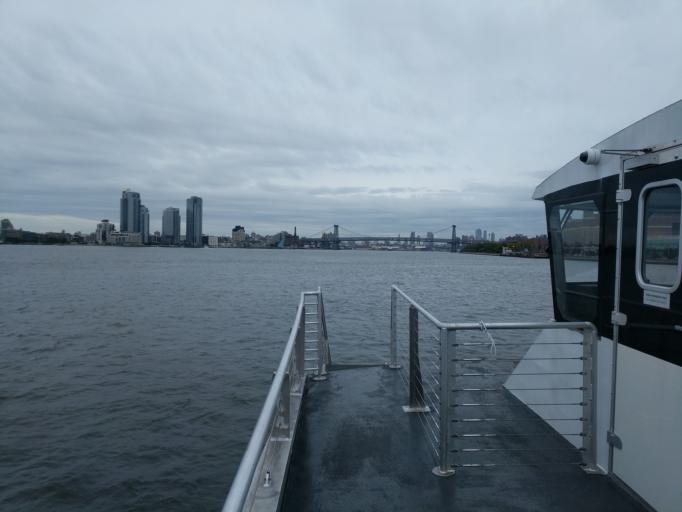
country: US
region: New York
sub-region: Queens County
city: Long Island City
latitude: 40.7319
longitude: -73.9691
